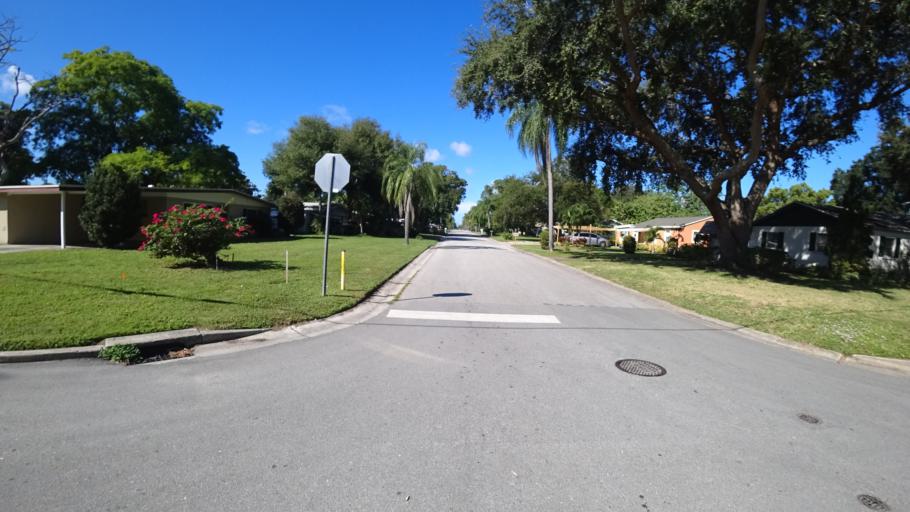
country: US
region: Florida
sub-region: Manatee County
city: South Bradenton
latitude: 27.4791
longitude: -82.5836
